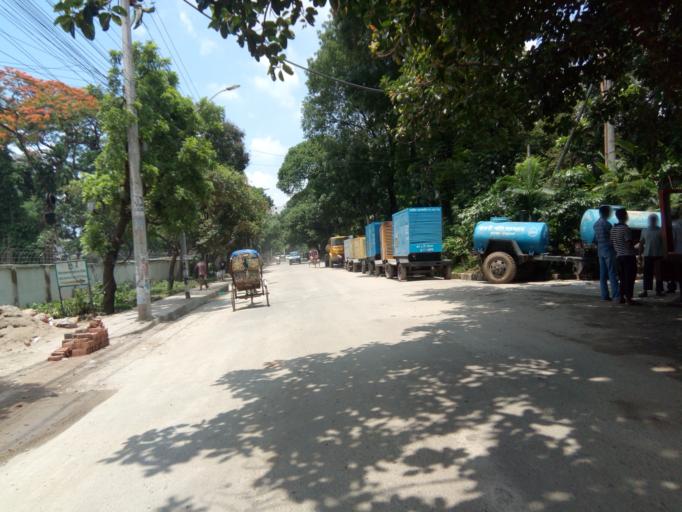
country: BD
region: Dhaka
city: Paltan
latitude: 23.7447
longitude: 90.4025
